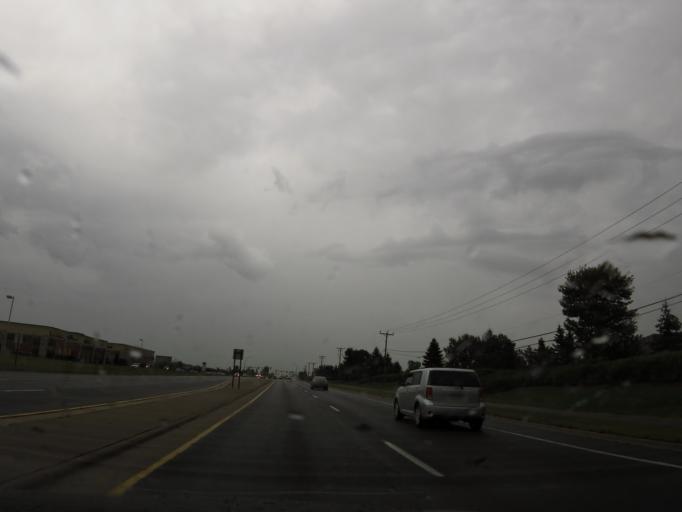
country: US
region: Minnesota
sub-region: Washington County
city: Woodbury
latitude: 44.9386
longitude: -92.9034
